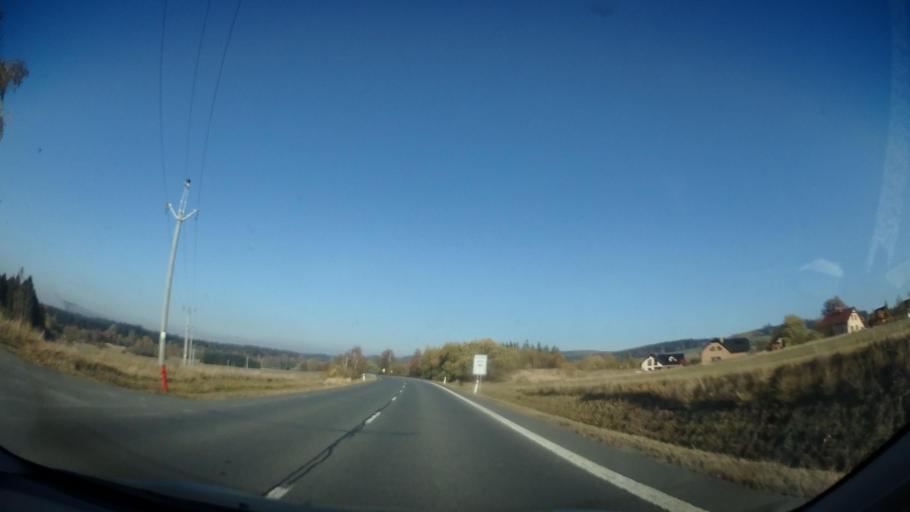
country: CZ
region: Vysocina
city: Zd'ar nad Sazavou Druhy
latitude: 49.6359
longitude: 15.9208
